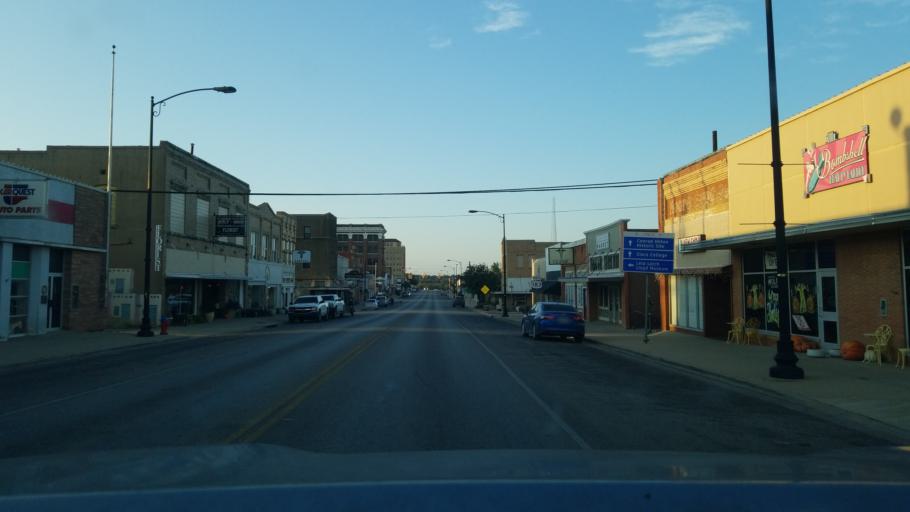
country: US
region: Texas
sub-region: Eastland County
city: Cisco
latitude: 32.3883
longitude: -98.9794
